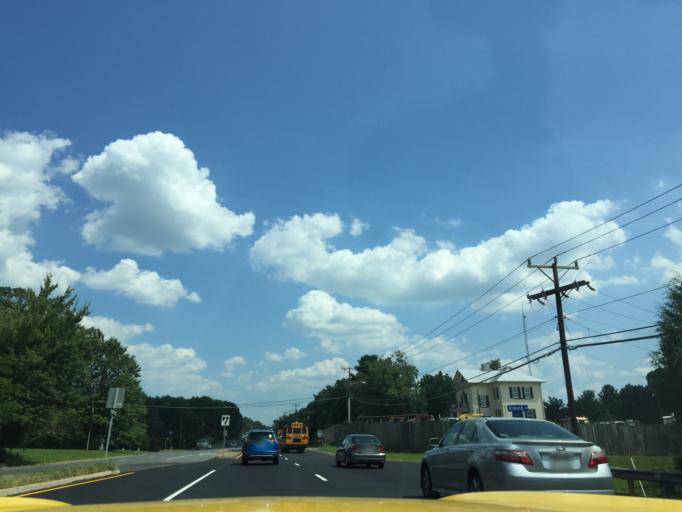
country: US
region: Virginia
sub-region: Fairfax County
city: Wolf Trap
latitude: 38.9547
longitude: -77.2698
